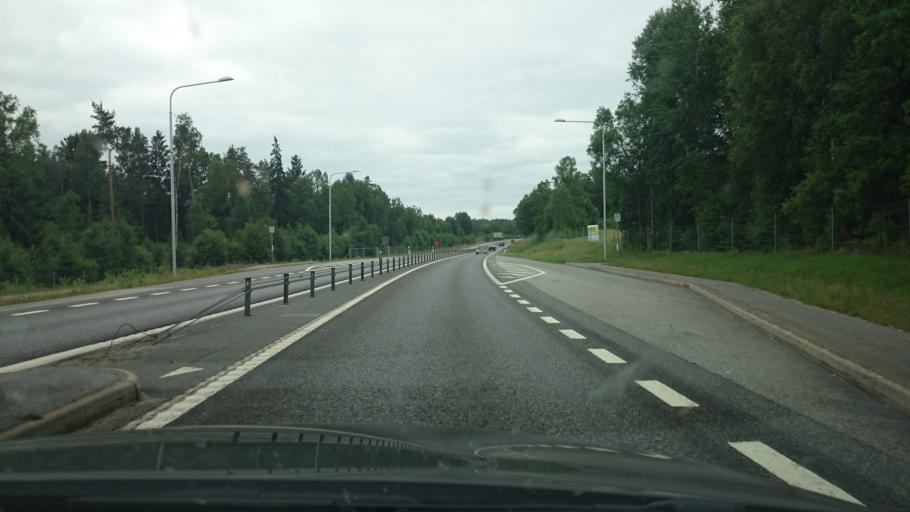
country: SE
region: Halland
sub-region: Hylte Kommun
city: Hyltebruk
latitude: 56.9876
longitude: 13.2163
